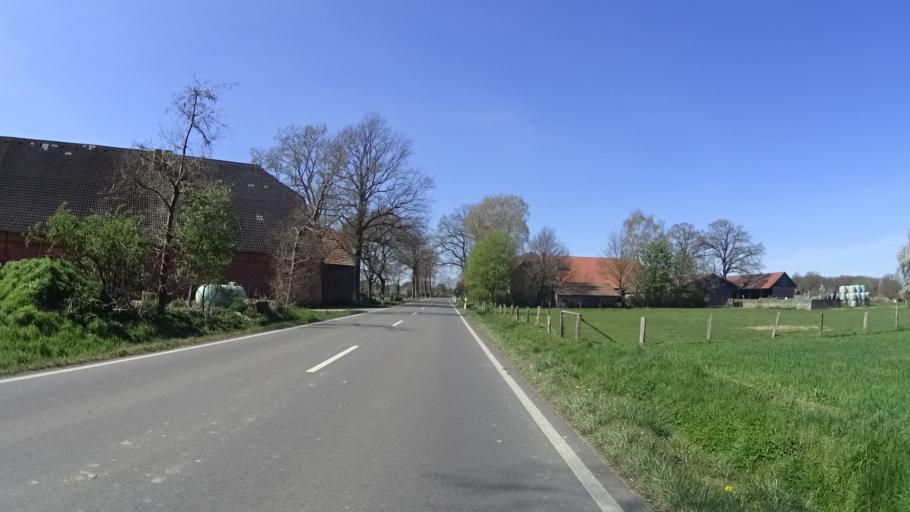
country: DE
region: North Rhine-Westphalia
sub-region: Regierungsbezirk Munster
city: Dulmen
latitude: 51.8217
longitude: 7.3697
